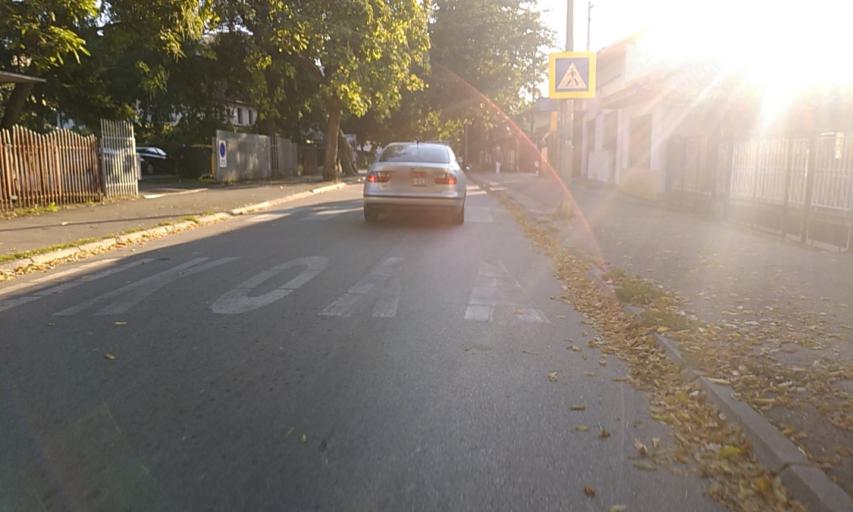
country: BA
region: Republika Srpska
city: Mejdan - Obilicevo
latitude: 44.7626
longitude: 17.1878
